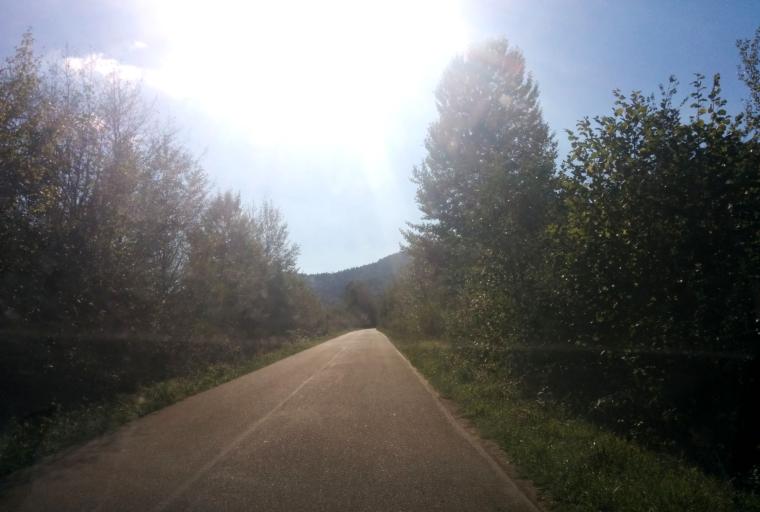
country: PL
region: Subcarpathian Voivodeship
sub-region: Powiat leski
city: Polanczyk
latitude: 49.2892
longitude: 22.4175
